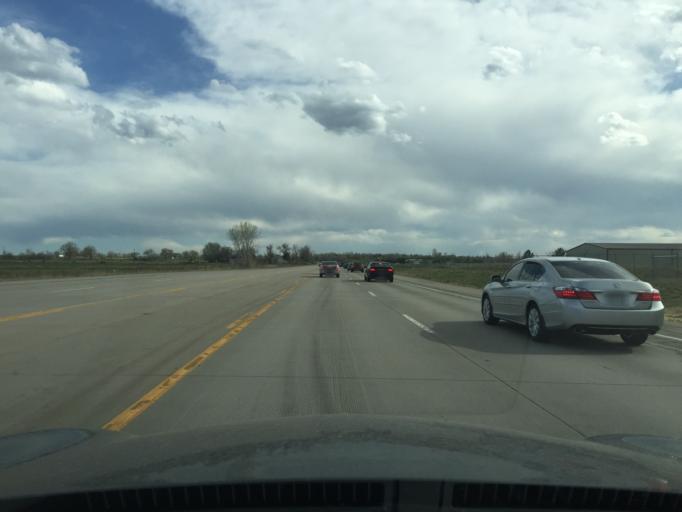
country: US
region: Colorado
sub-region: Boulder County
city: Lafayette
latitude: 40.0417
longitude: -105.1027
